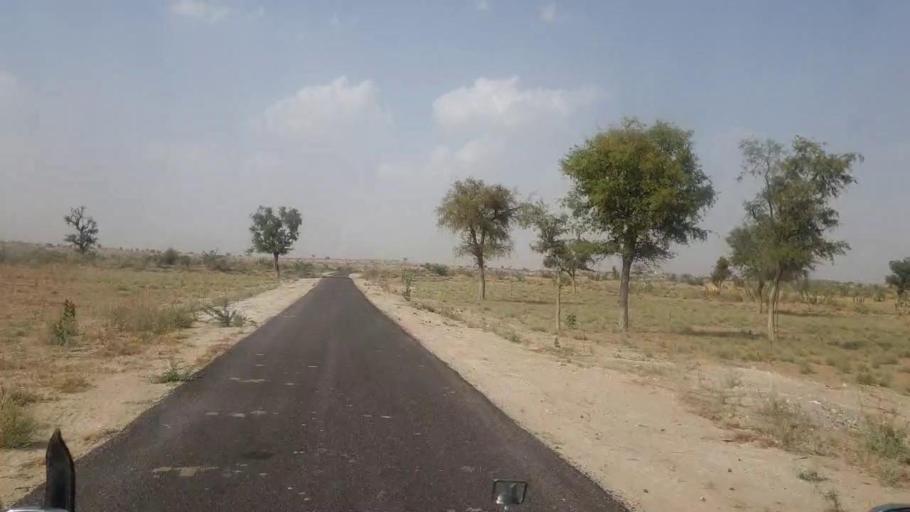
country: PK
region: Sindh
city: Islamkot
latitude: 25.2020
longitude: 70.2837
